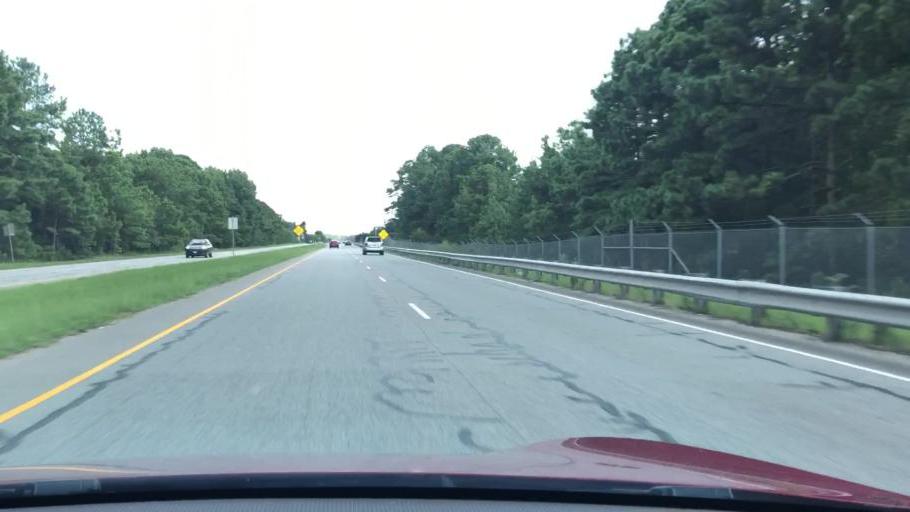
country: US
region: Virginia
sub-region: City of Virginia Beach
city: Virginia Beach
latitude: 36.8315
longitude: -76.0115
